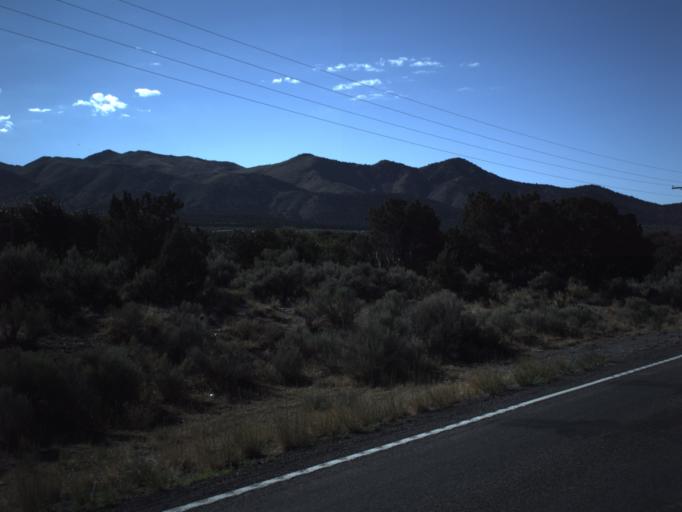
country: US
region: Utah
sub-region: Juab County
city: Mona
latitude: 39.8768
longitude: -112.1381
